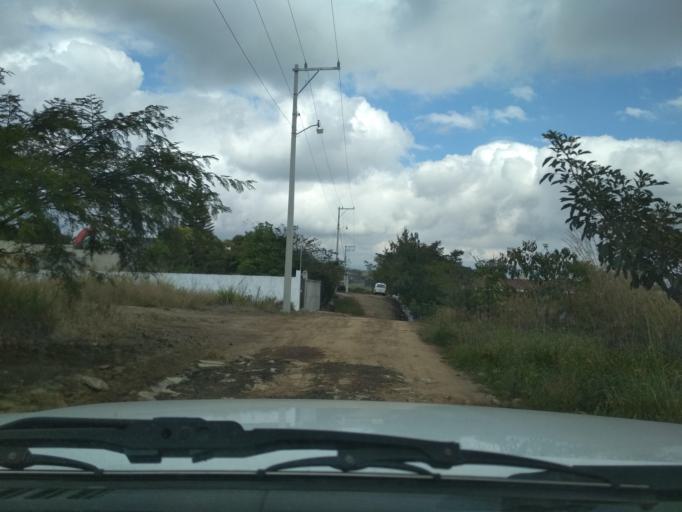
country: MX
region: Veracruz
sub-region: Emiliano Zapata
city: Dos Rios
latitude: 19.5019
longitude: -96.8217
